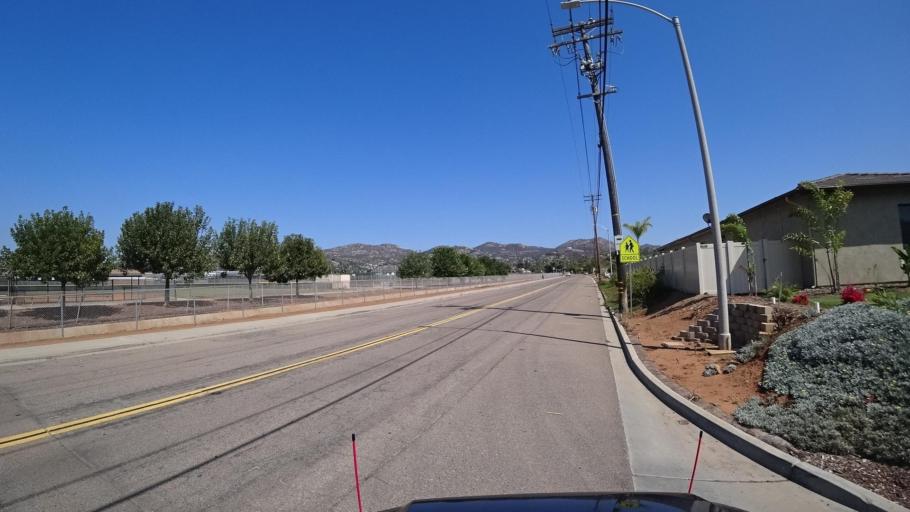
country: US
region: California
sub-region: San Diego County
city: Granite Hills
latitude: 32.7963
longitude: -116.9166
